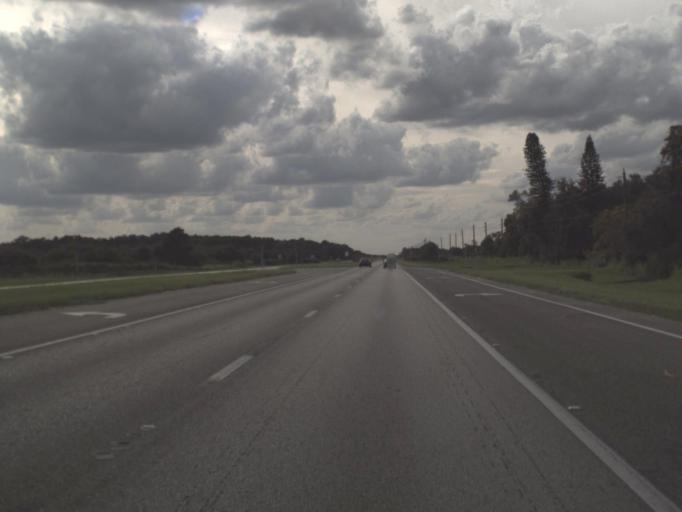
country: US
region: Florida
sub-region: Lee County
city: Alva
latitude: 26.7097
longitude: -81.5613
